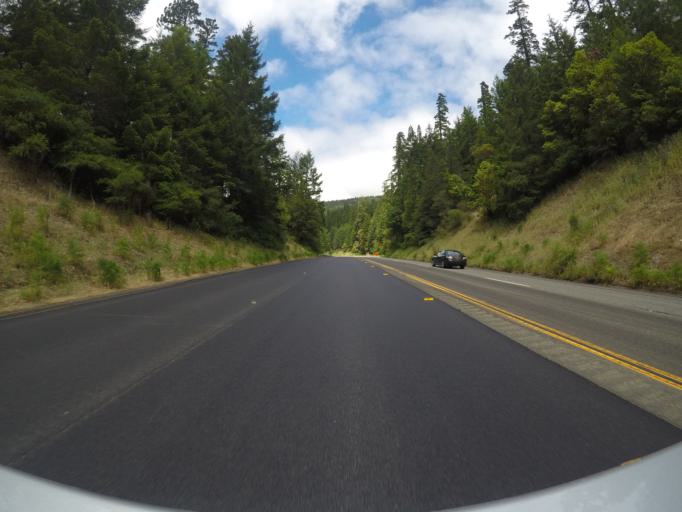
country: US
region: California
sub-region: Humboldt County
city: Redway
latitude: 40.2961
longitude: -123.8929
